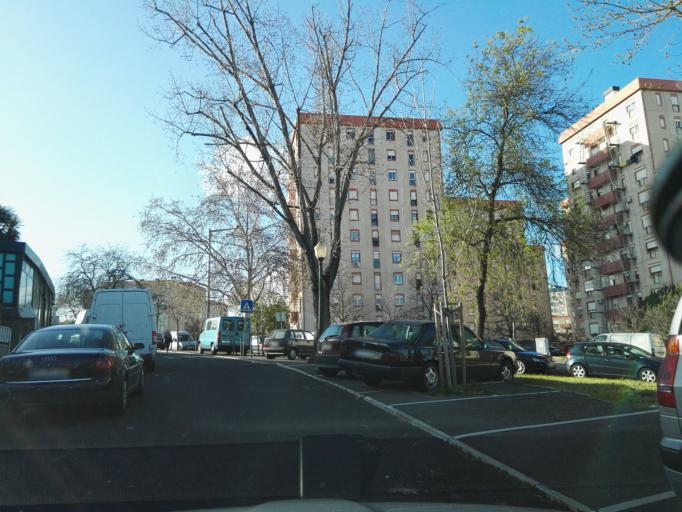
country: PT
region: Lisbon
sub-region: Loures
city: Moscavide
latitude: 38.7777
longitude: -9.1183
